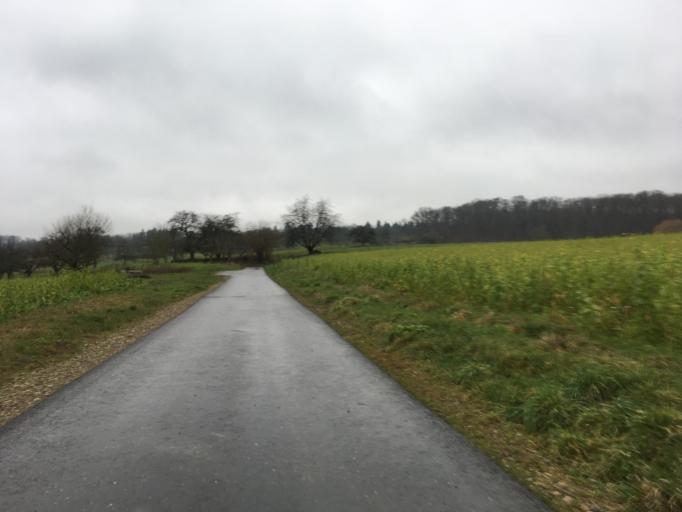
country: DE
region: Baden-Wuerttemberg
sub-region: Karlsruhe Region
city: Konigsbach-Stein
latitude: 48.9470
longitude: 8.5284
